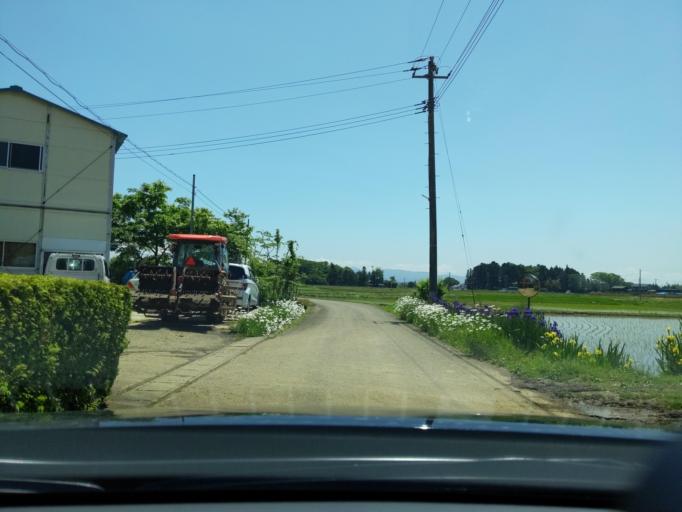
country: JP
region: Fukushima
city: Koriyama
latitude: 37.3876
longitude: 140.2912
